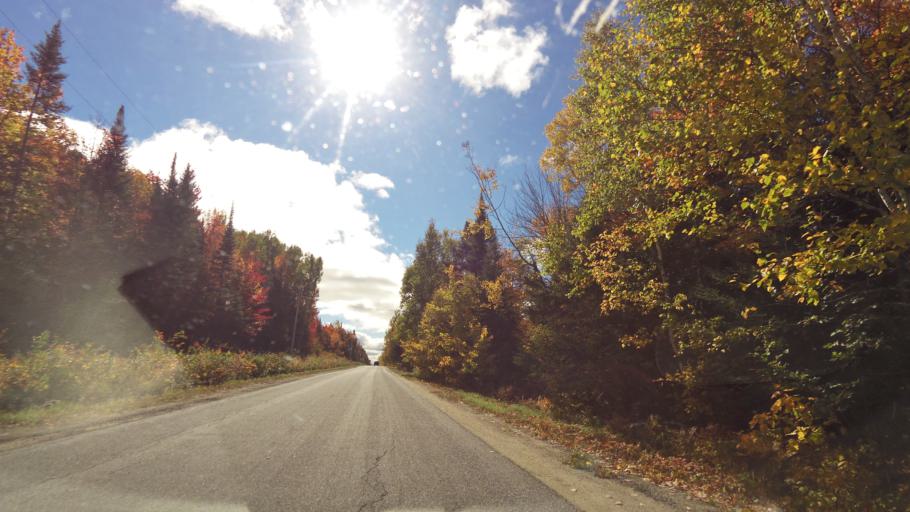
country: CA
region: Ontario
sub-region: Nipissing District
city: North Bay
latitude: 46.3568
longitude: -79.4872
